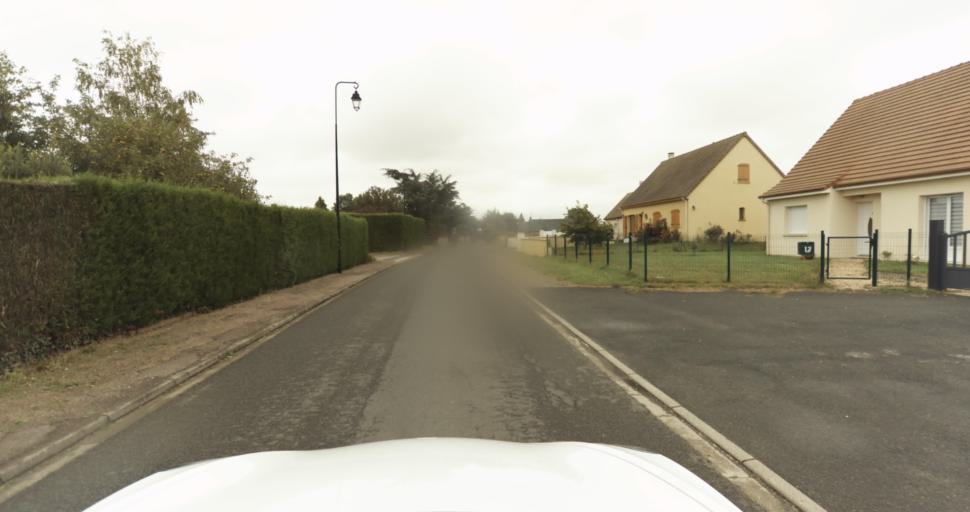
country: FR
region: Haute-Normandie
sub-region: Departement de l'Eure
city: Aviron
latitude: 49.0815
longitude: 1.0755
